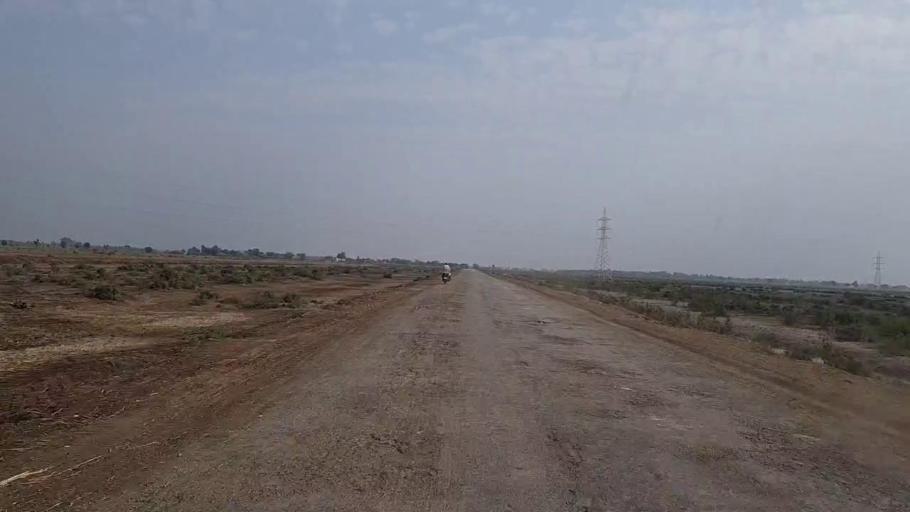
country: PK
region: Sindh
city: Mirpur Khas
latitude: 25.4208
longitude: 69.0260
